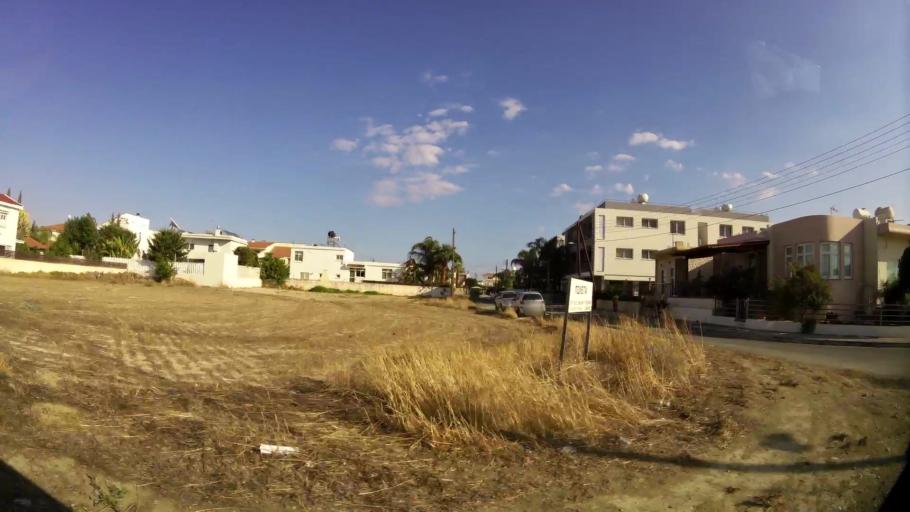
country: CY
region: Larnaka
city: Aradippou
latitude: 34.9423
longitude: 33.6004
